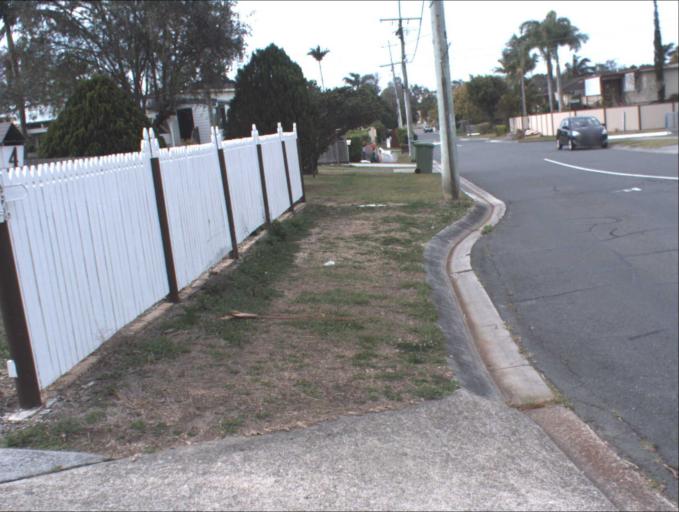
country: AU
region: Queensland
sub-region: Logan
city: Logan City
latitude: -27.6323
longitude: 153.1235
